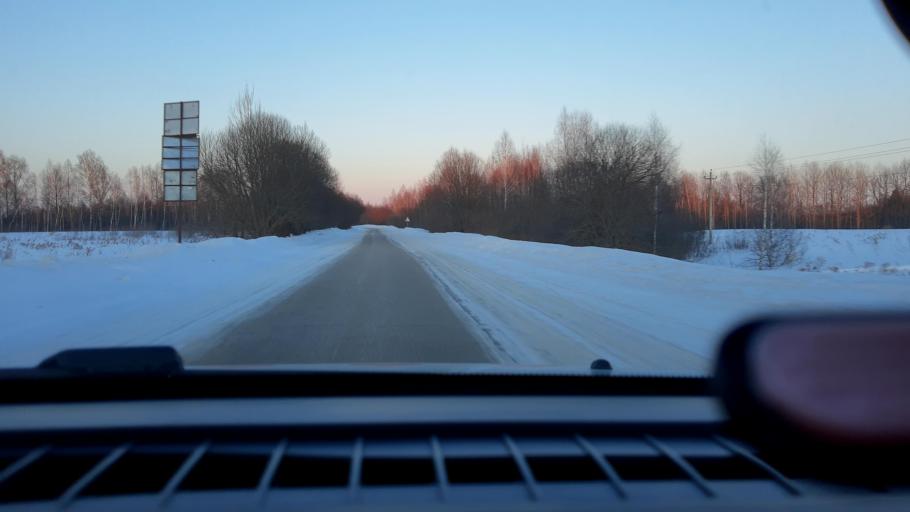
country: RU
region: Nizjnij Novgorod
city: Lyskovo
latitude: 56.1446
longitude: 45.1175
